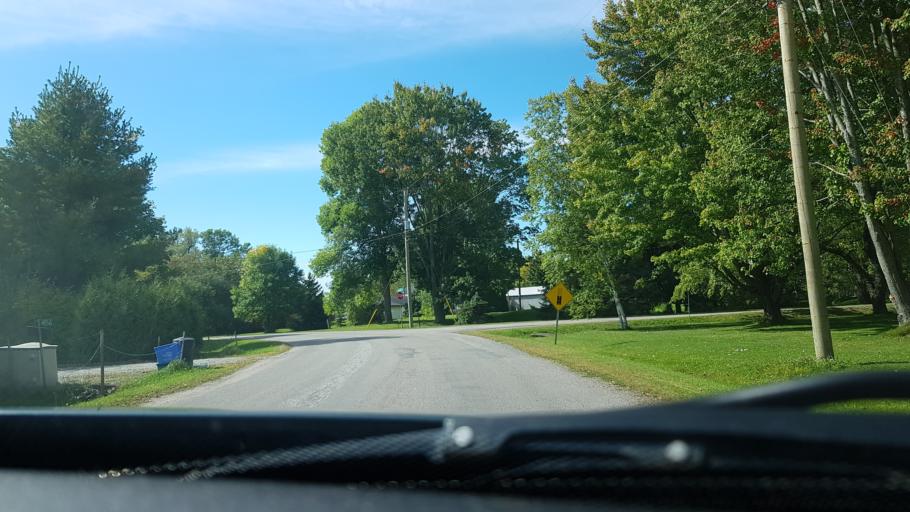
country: CA
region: Ontario
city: Orillia
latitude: 44.5949
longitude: -79.3227
